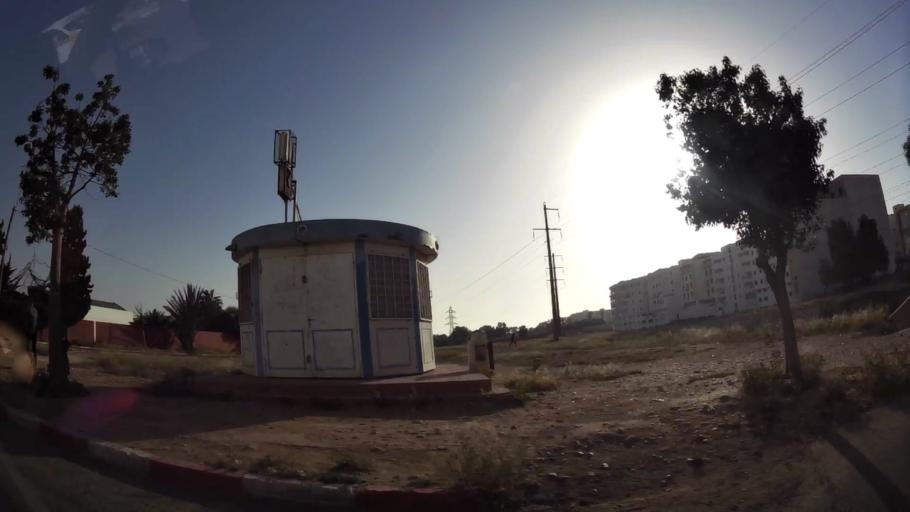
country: MA
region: Souss-Massa-Draa
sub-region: Agadir-Ida-ou-Tnan
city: Agadir
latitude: 30.4094
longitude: -9.5822
